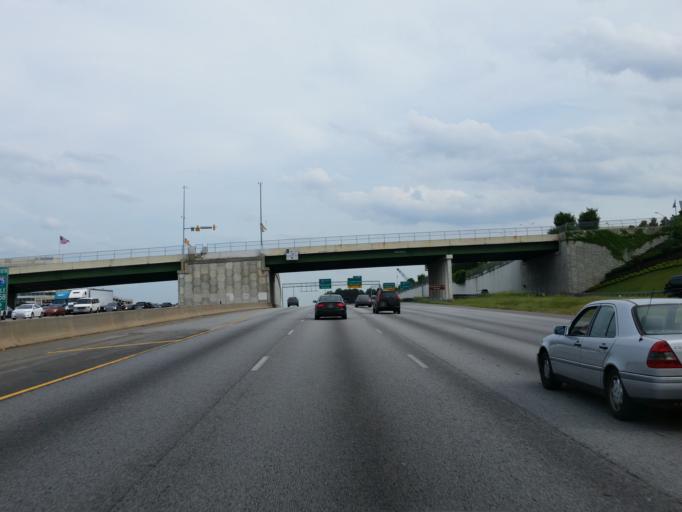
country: US
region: Georgia
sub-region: Cobb County
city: Vinings
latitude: 33.8874
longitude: -84.4589
